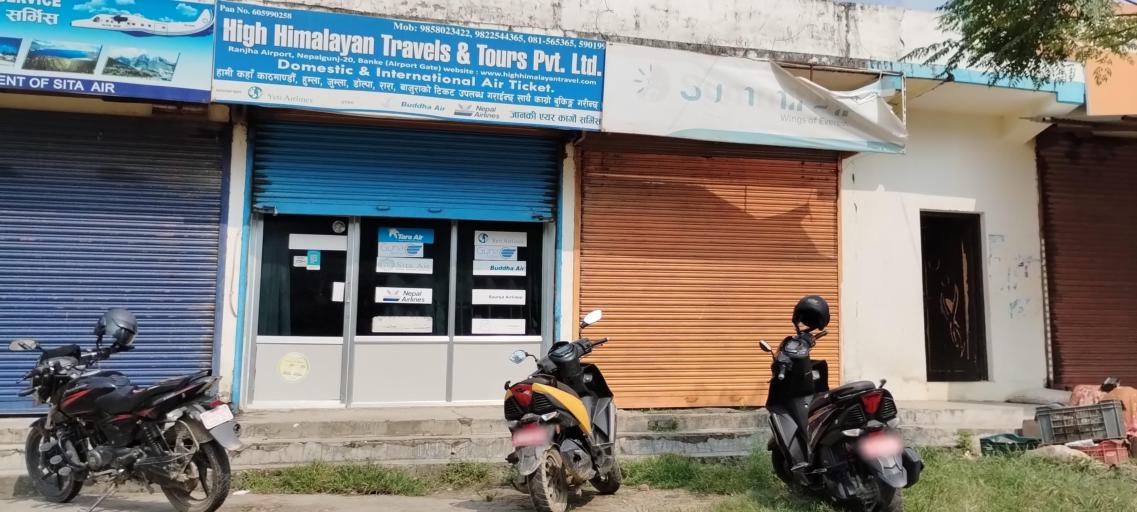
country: NP
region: Mid Western
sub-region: Bheri Zone
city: Nepalgunj
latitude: 28.0996
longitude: 81.6660
